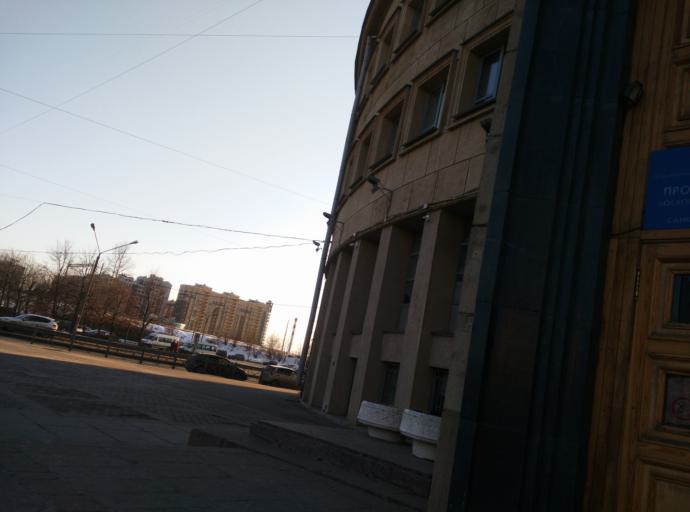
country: RU
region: St.-Petersburg
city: Admiralteisky
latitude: 59.8845
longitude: 30.3195
